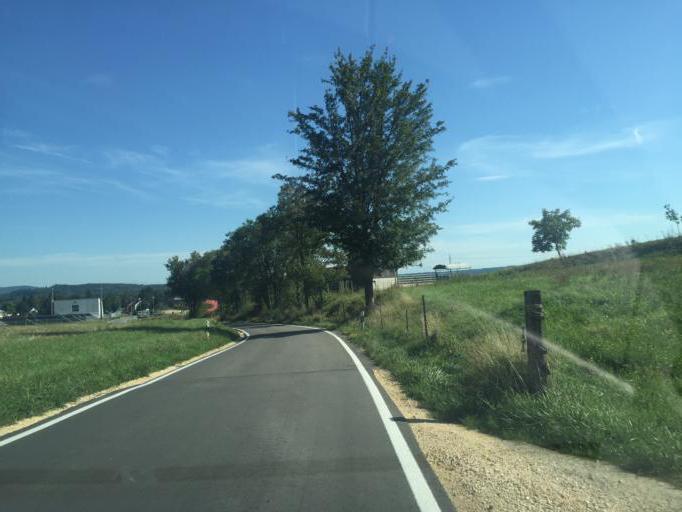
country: DE
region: Baden-Wuerttemberg
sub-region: Freiburg Region
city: Busingen
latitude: 47.7018
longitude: 8.6849
